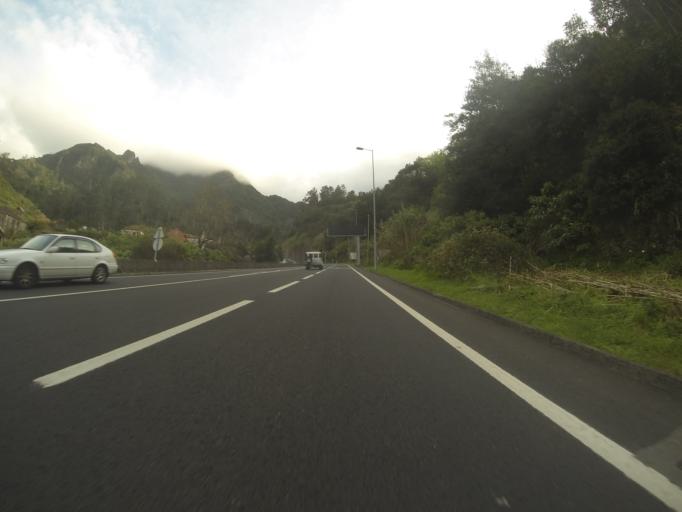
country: PT
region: Madeira
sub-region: Sao Vicente
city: Sao Vicente
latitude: 32.7704
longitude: -17.0302
